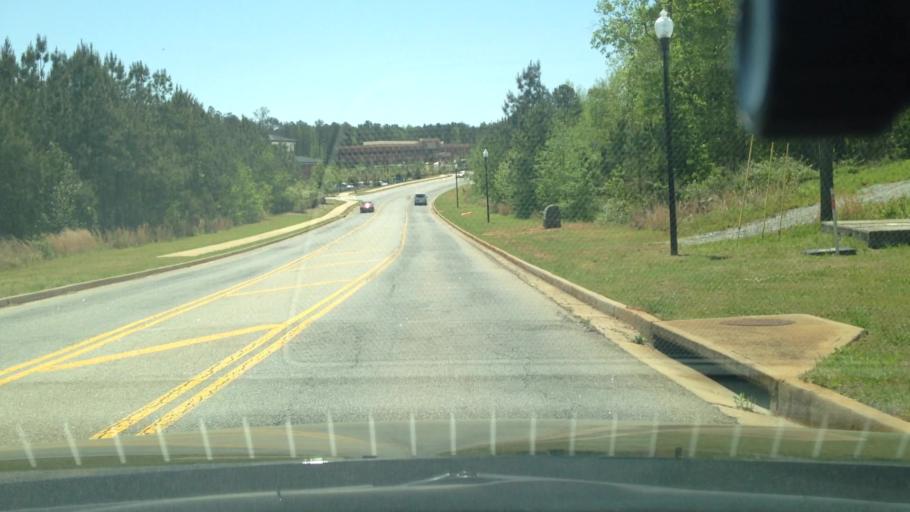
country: US
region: Georgia
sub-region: Coweta County
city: East Newnan
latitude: 33.3641
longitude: -84.7539
